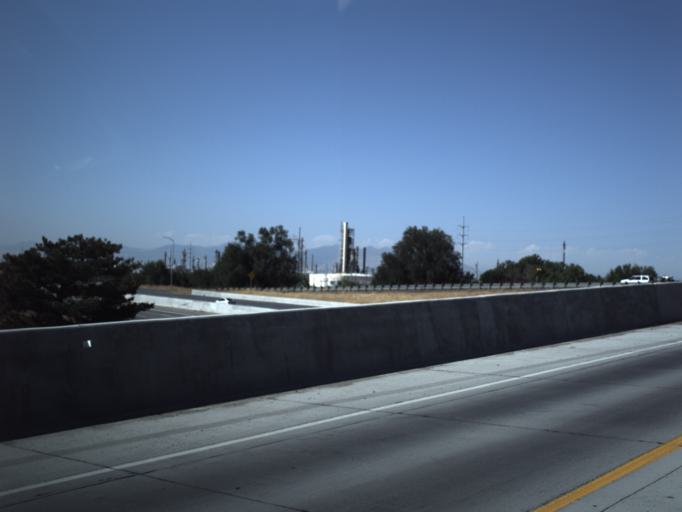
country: US
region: Utah
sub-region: Davis County
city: West Bountiful
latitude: 40.8939
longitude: -111.8952
